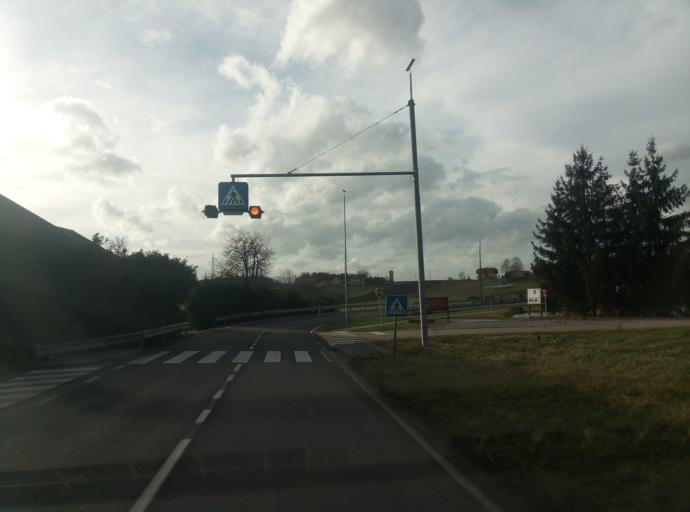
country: SI
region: Celje
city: Ljubecna
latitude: 46.2380
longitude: 15.3523
